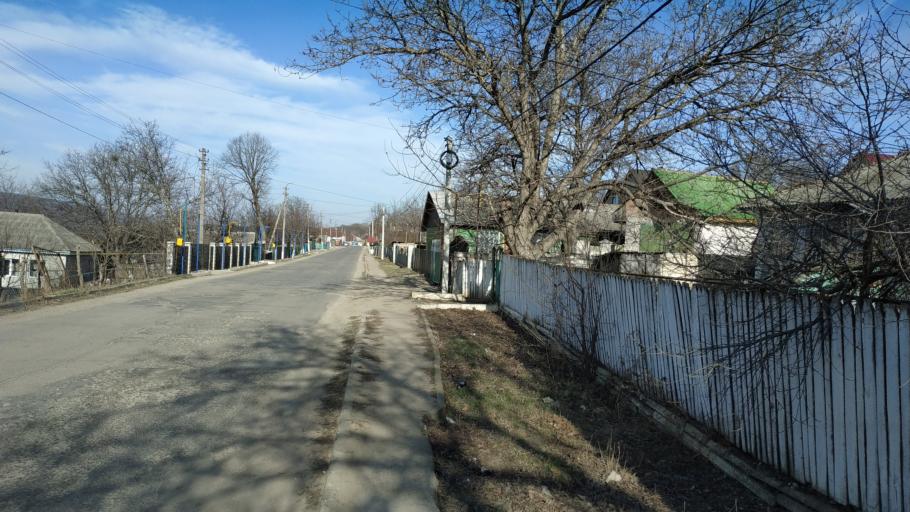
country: MD
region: Chisinau
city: Vatra
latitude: 47.0233
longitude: 28.6412
